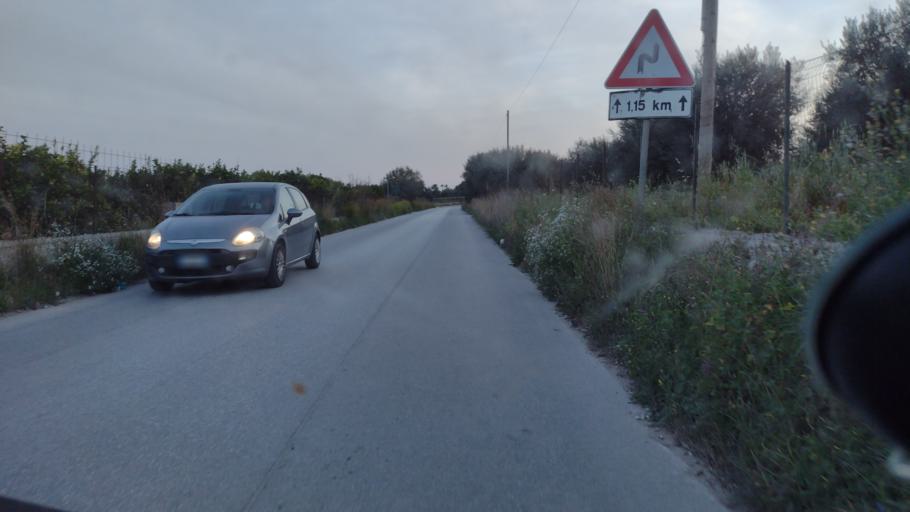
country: IT
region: Sicily
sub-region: Provincia di Siracusa
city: Avola
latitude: 36.8919
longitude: 15.1330
